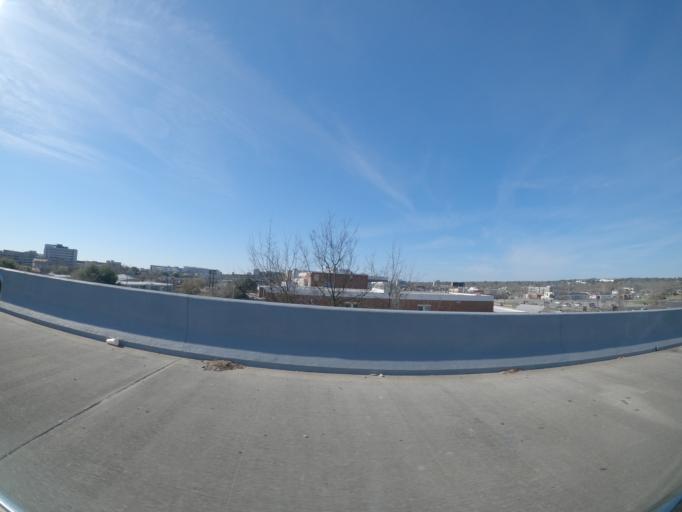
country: US
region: Georgia
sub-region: Richmond County
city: Augusta
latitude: 33.4770
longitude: -81.9841
